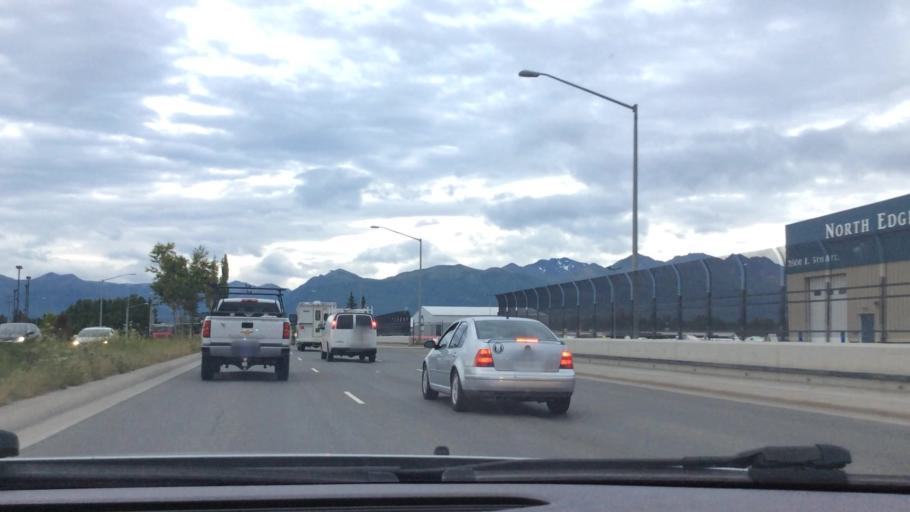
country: US
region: Alaska
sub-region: Anchorage Municipality
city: Anchorage
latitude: 61.2181
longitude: -149.8303
